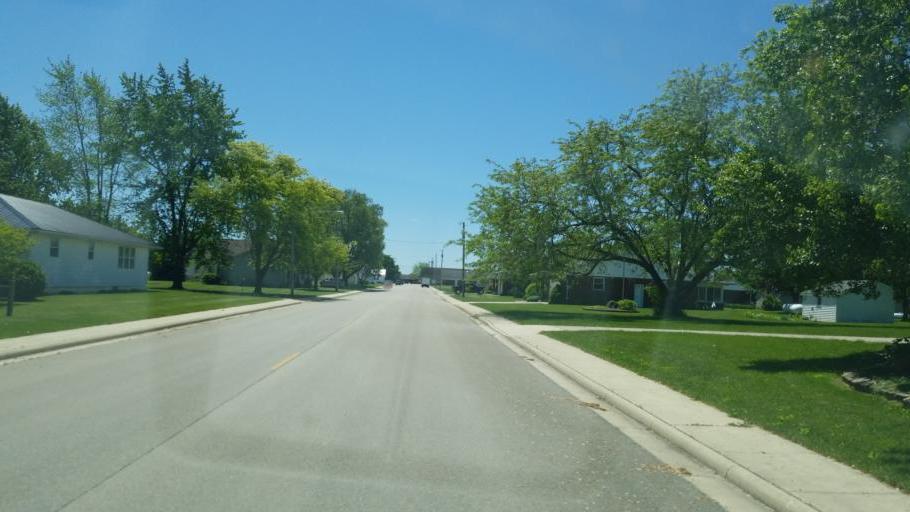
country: US
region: Ohio
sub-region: Mercer County
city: Saint Henry
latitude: 40.3546
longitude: -84.6429
